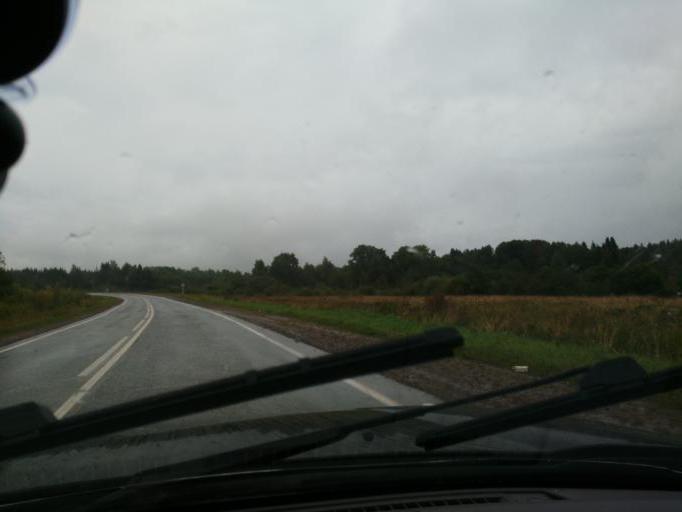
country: RU
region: Perm
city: Osa
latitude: 57.3953
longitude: 55.6179
